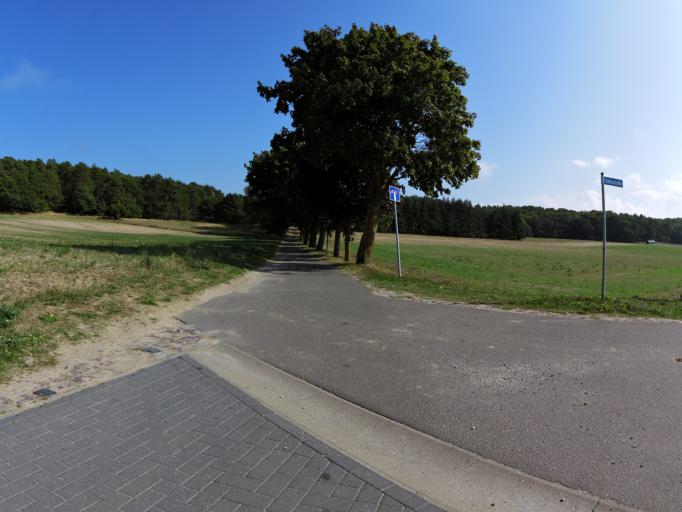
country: DE
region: Mecklenburg-Vorpommern
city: Loddin
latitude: 54.0084
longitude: 14.0474
